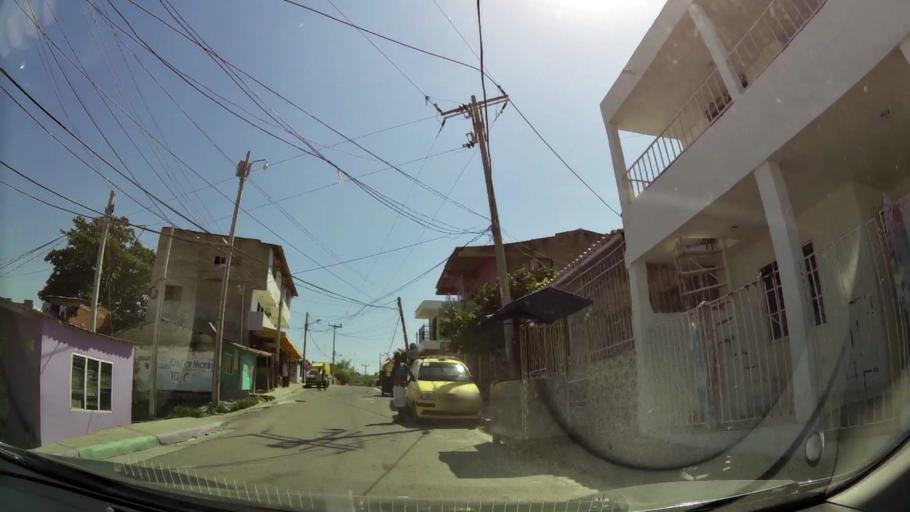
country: CO
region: Bolivar
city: Cartagena
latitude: 10.4317
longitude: -75.5262
